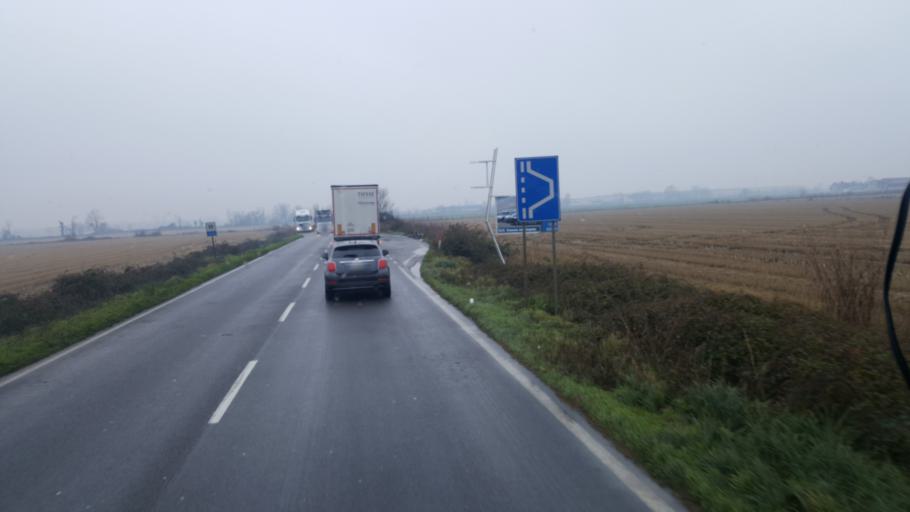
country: IT
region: Lombardy
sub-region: Citta metropolitana di Milano
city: Locate di Triulzi
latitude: 45.3291
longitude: 9.2288
